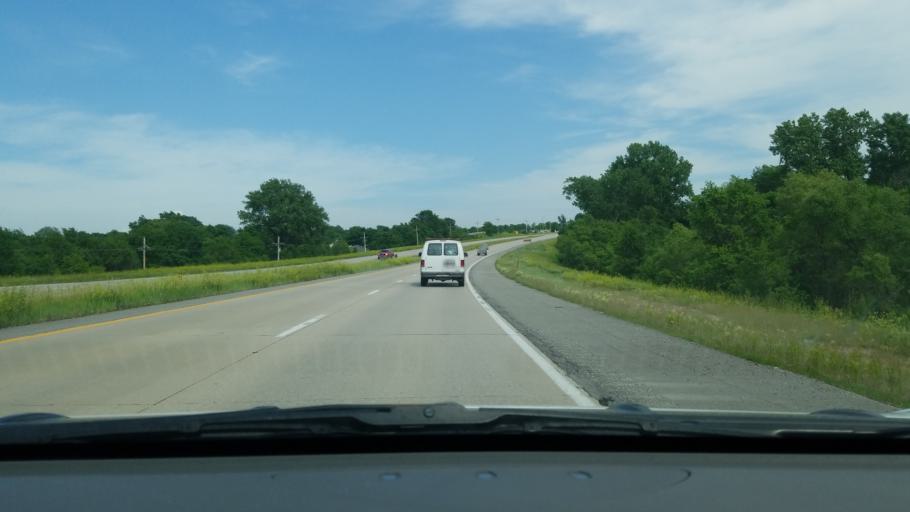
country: US
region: Nebraska
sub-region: Sarpy County
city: Papillion
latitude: 41.1470
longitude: -96.0690
